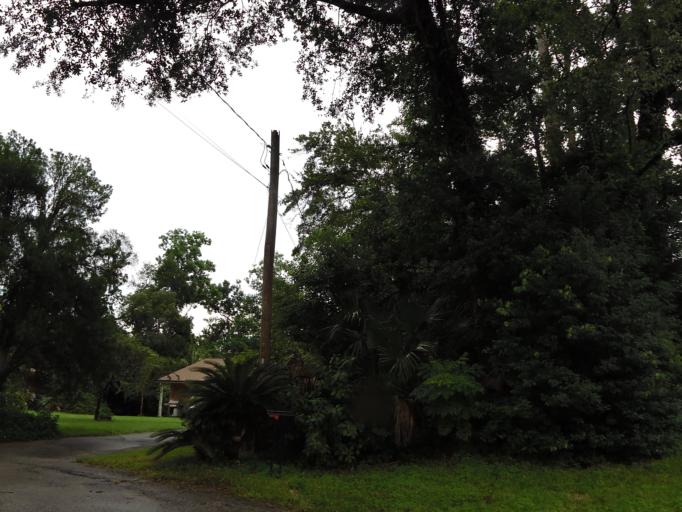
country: US
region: Florida
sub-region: Duval County
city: Jacksonville
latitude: 30.2914
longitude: -81.5936
